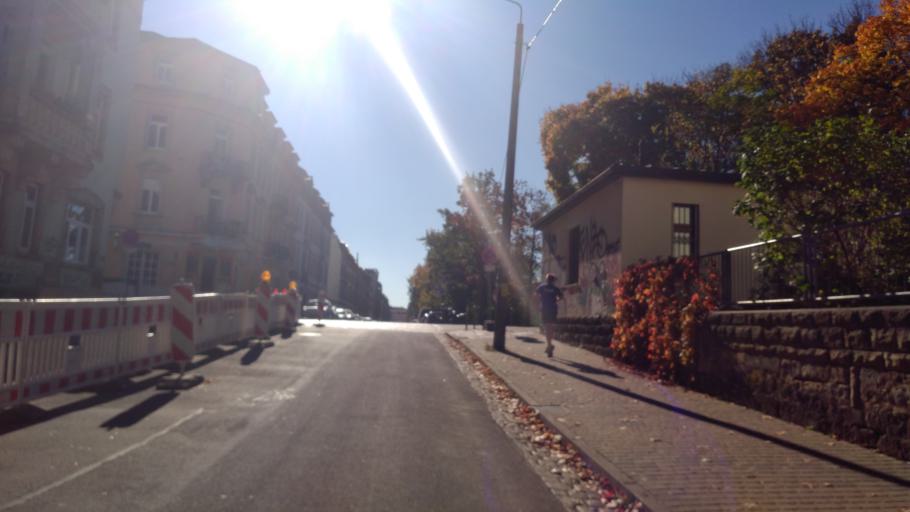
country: DE
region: Saxony
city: Albertstadt
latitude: 51.0706
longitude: 13.7602
